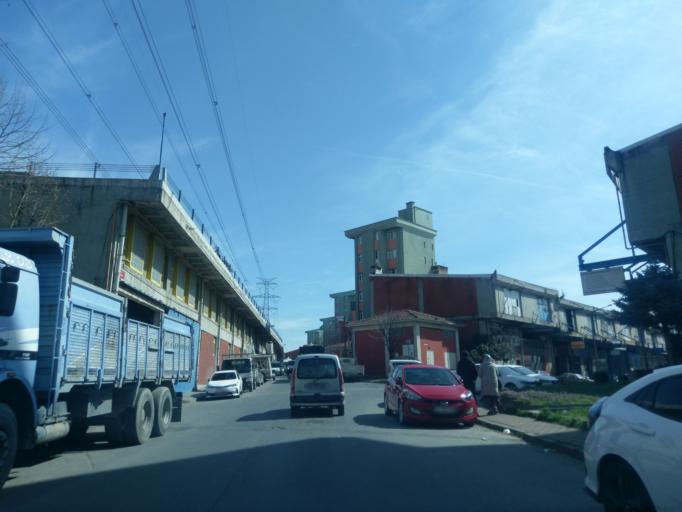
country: TR
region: Istanbul
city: Basaksehir
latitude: 41.0698
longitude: 28.7984
